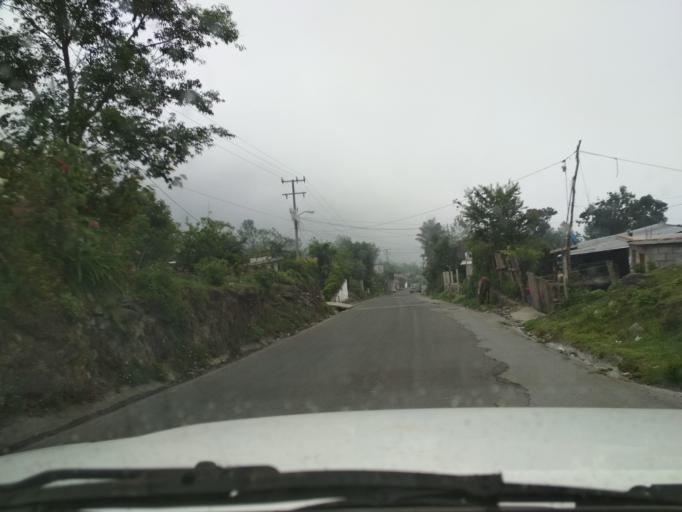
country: MX
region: Veracruz
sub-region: Mariano Escobedo
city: San Isidro el Berro
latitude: 18.9540
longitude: -97.1796
